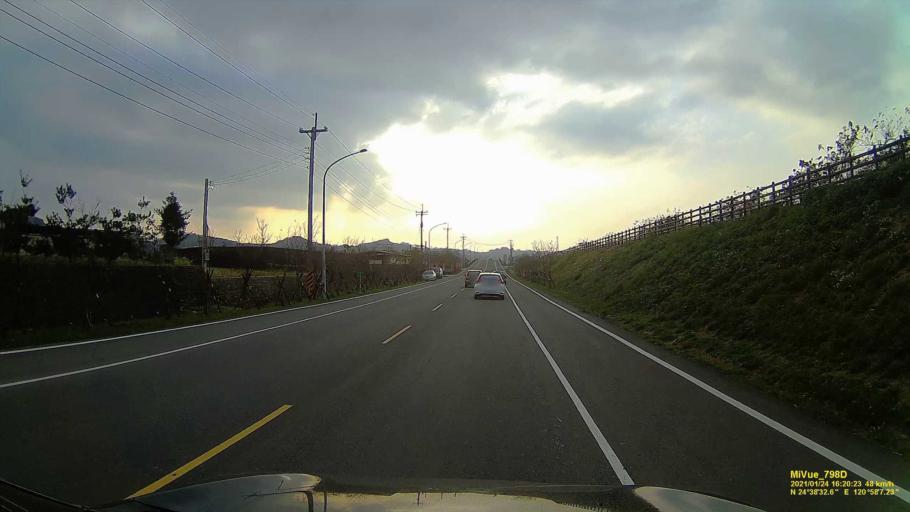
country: TW
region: Taiwan
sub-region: Hsinchu
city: Hsinchu
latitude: 24.6422
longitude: 120.9679
